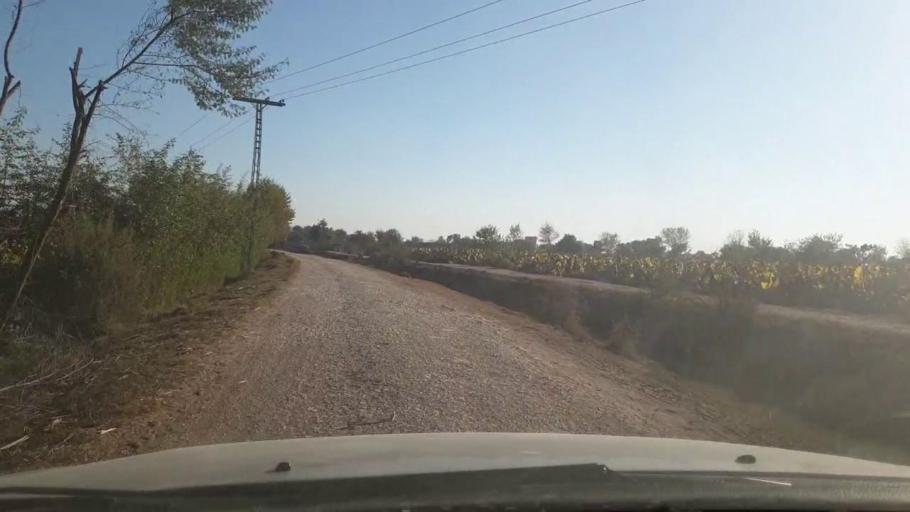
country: PK
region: Sindh
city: Adilpur
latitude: 27.9452
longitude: 69.2187
